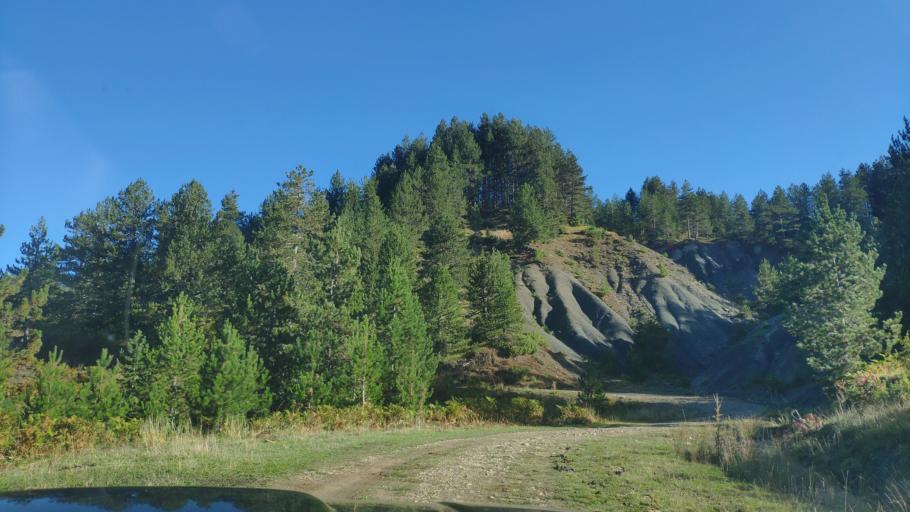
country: GR
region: Epirus
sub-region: Nomos Ioanninon
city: Metsovo
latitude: 39.8353
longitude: 21.1340
